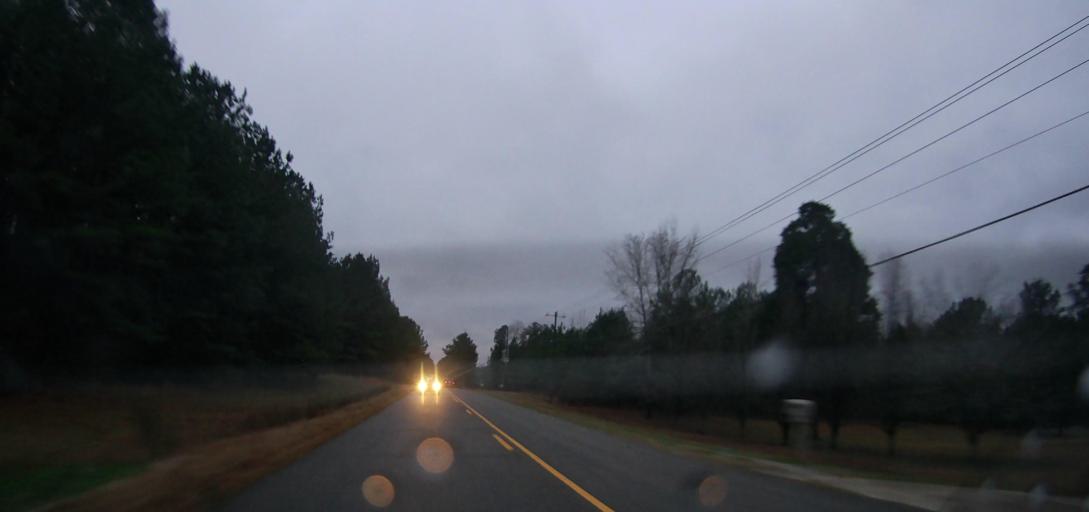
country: US
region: Alabama
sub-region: Tuscaloosa County
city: Vance
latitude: 33.1442
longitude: -87.2298
